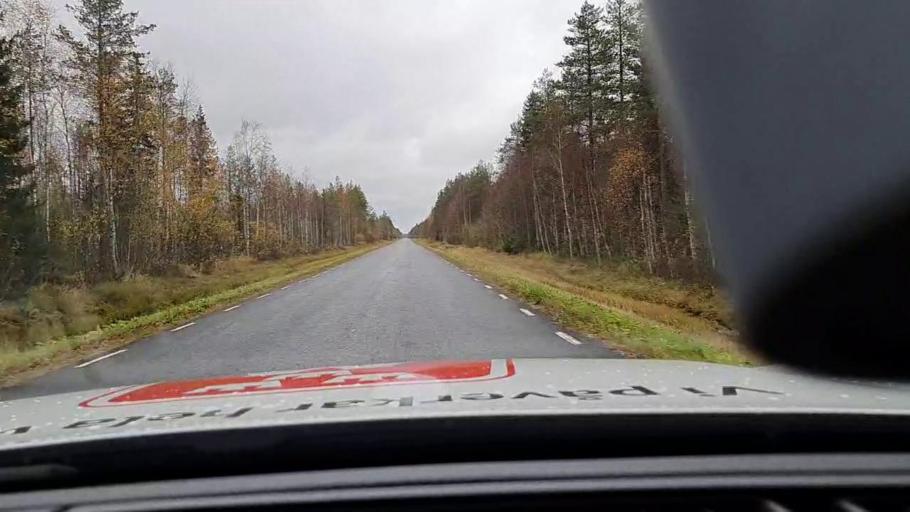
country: SE
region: Norrbotten
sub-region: Haparanda Kommun
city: Haparanda
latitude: 65.9053
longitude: 23.8329
